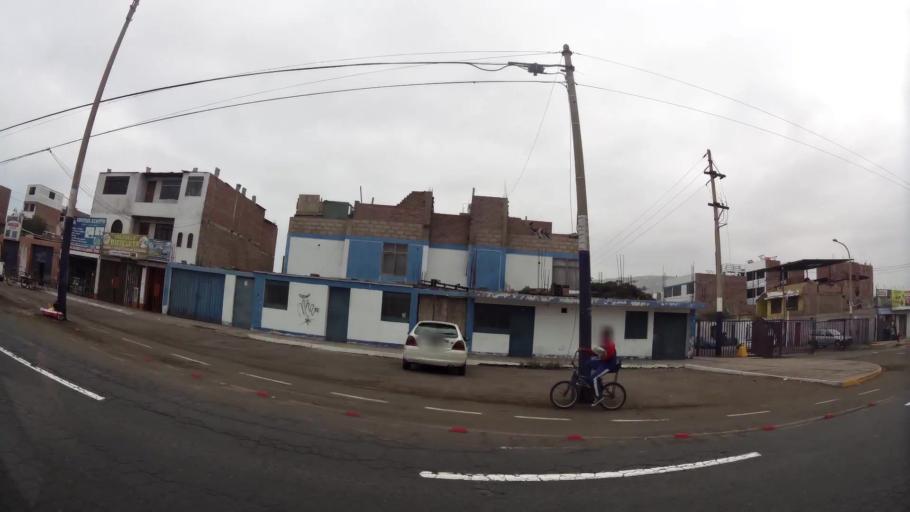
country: PE
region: Lima
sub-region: Lima
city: Surco
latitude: -12.2033
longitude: -77.0160
